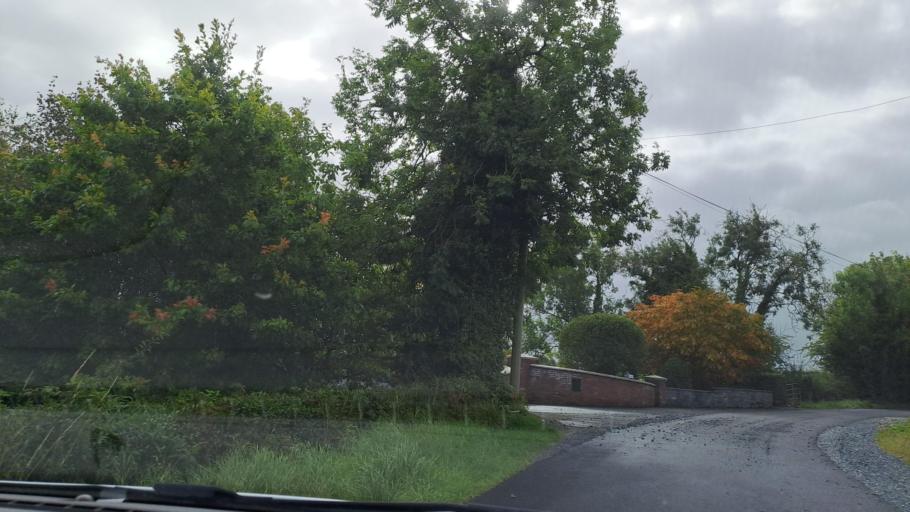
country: IE
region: Ulster
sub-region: County Monaghan
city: Carrickmacross
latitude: 53.9861
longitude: -6.7767
